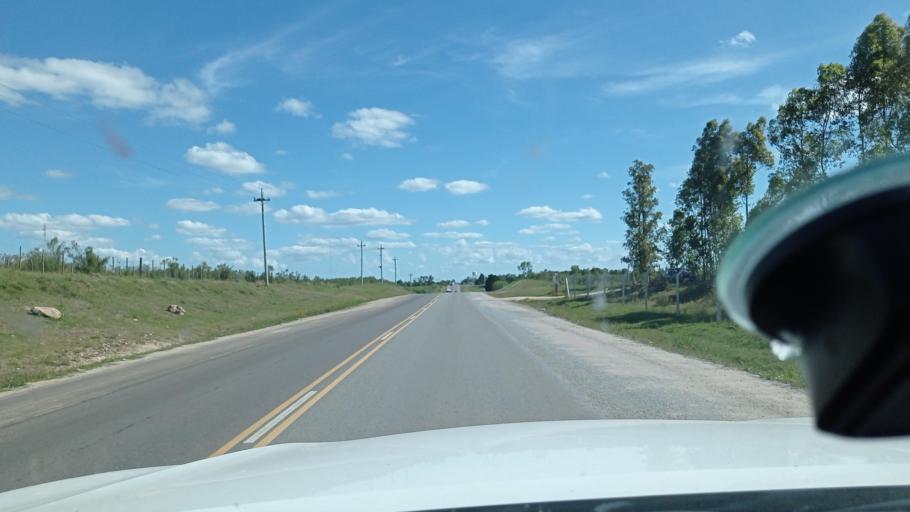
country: UY
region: Florida
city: Florida
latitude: -34.0778
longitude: -56.2347
